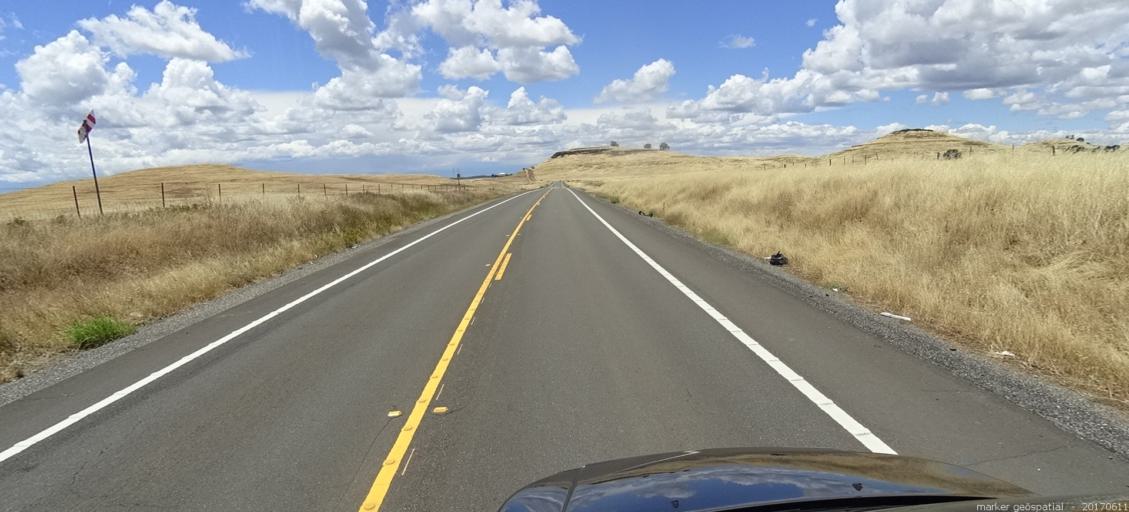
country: US
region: California
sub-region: Butte County
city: Paradise
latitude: 39.6394
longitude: -121.6697
